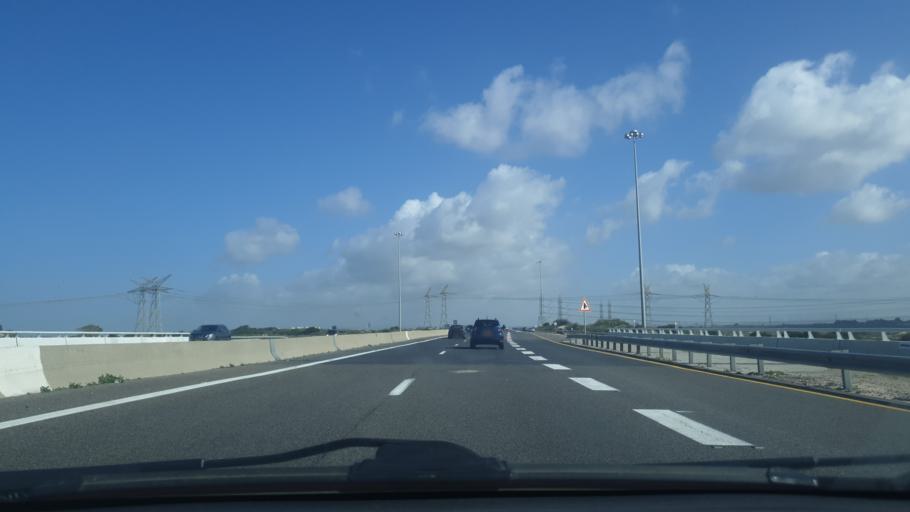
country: IL
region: Haifa
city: Hadera
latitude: 32.4717
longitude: 34.8996
